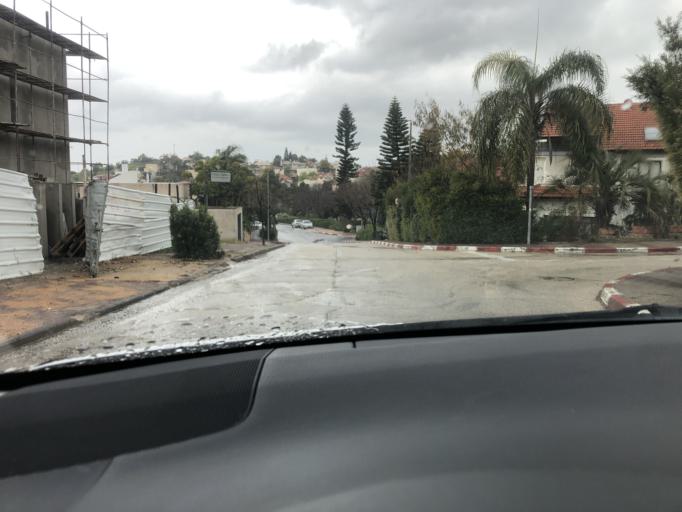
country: PS
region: West Bank
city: Azun Atme
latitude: 32.1112
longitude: 35.0301
